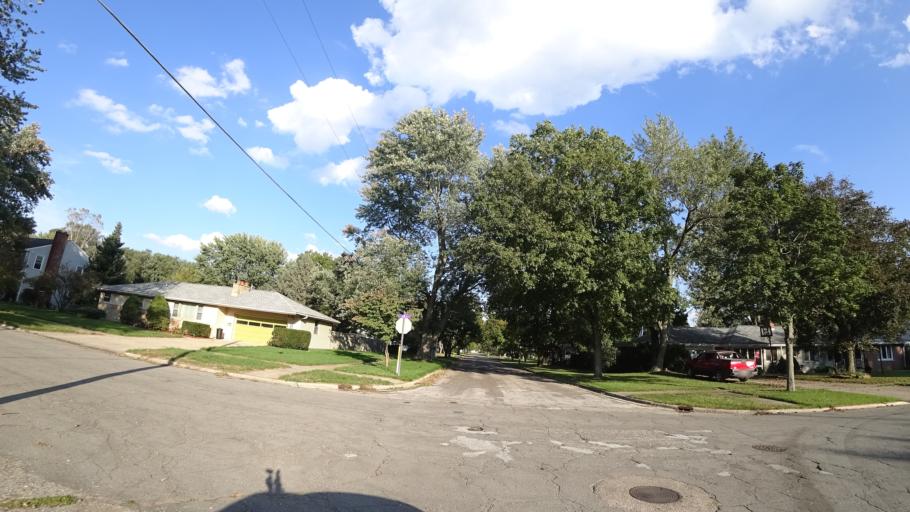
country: US
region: Michigan
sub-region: Saint Joseph County
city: Three Rivers
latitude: 41.9574
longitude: -85.6310
